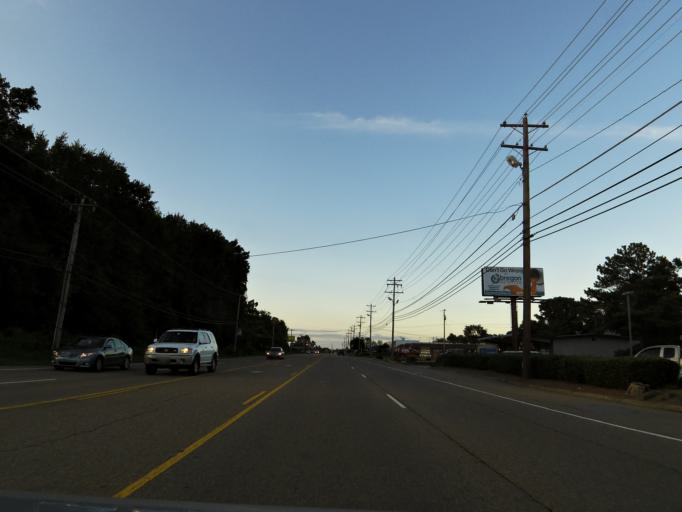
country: US
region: Tennessee
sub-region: Knox County
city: Farragut
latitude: 35.8881
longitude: -84.1489
